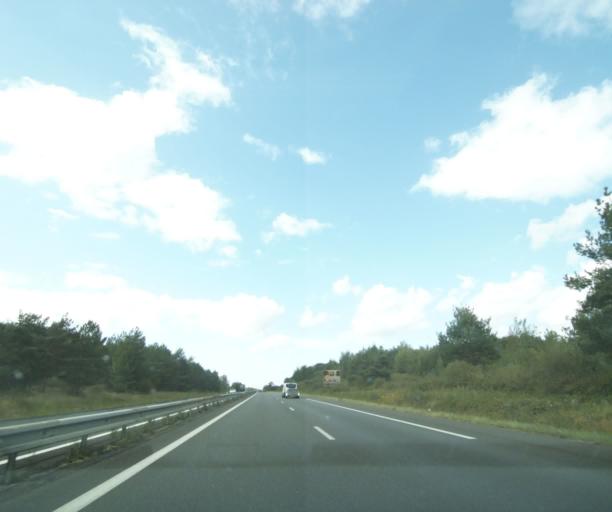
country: FR
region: Centre
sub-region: Departement du Loiret
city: La Ferte-Saint-Aubin
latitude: 47.7330
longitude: 1.8770
